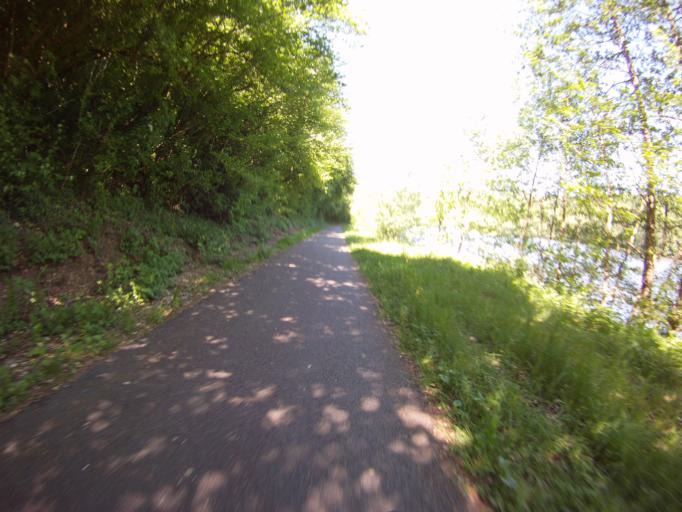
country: FR
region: Lorraine
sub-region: Departement de Meurthe-et-Moselle
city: Velaine-en-Haye
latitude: 48.6570
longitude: 6.0254
